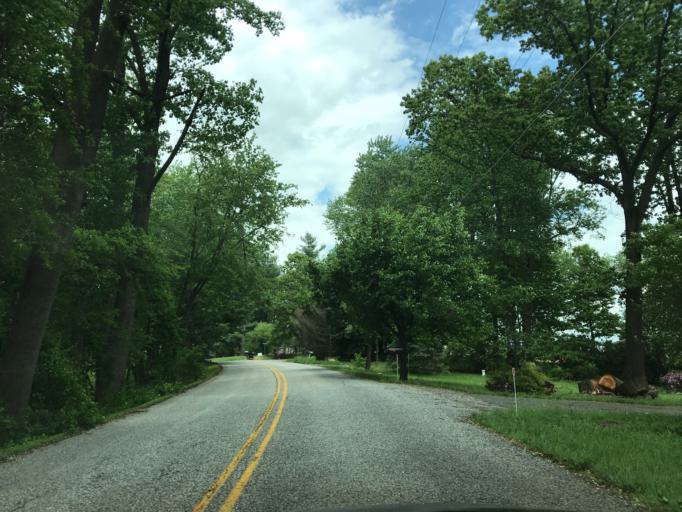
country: US
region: Maryland
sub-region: Harford County
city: Bel Air North
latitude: 39.6107
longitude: -76.3608
